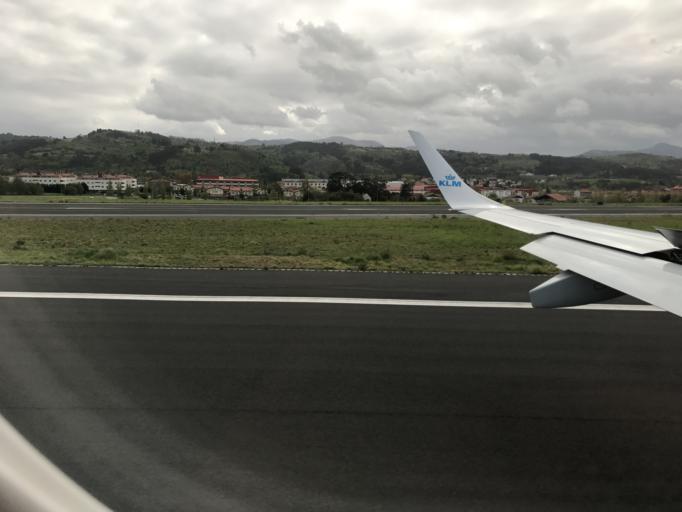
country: ES
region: Basque Country
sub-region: Bizkaia
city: Sondika
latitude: 43.3023
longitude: -2.9141
